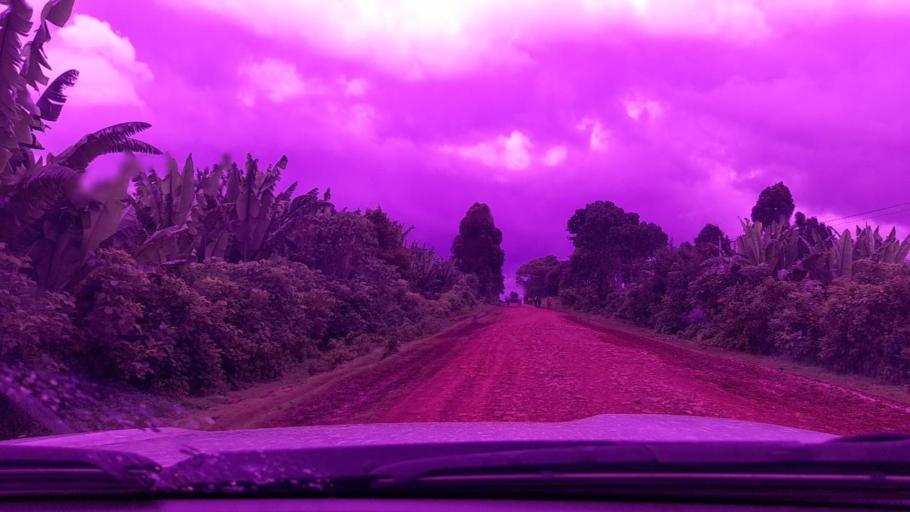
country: ET
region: Southern Nations, Nationalities, and People's Region
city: Tippi
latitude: 7.5768
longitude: 35.6341
